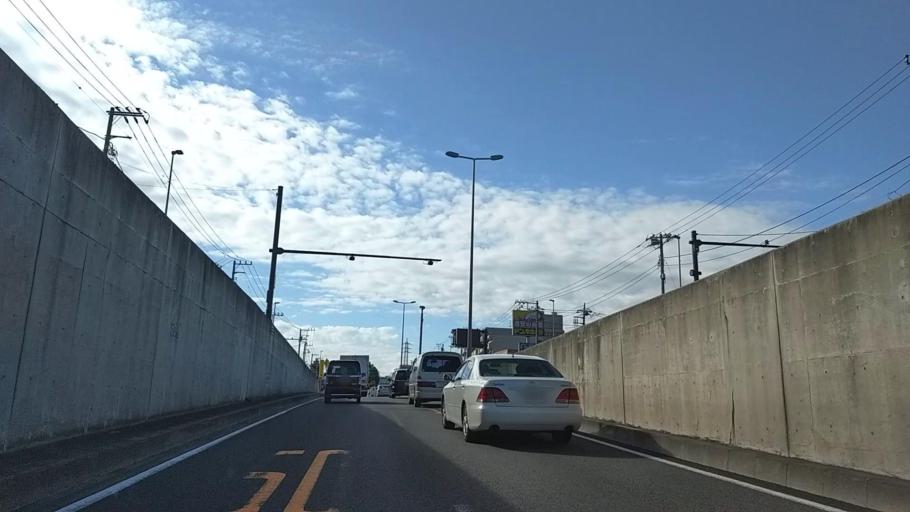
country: JP
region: Kanagawa
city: Fujisawa
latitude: 35.3762
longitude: 139.5047
